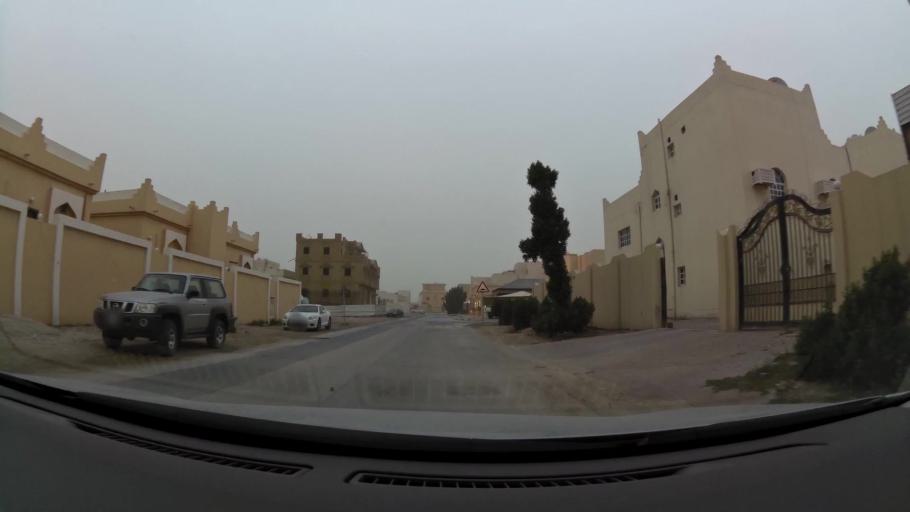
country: QA
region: Baladiyat ad Dawhah
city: Doha
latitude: 25.2358
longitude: 51.4978
